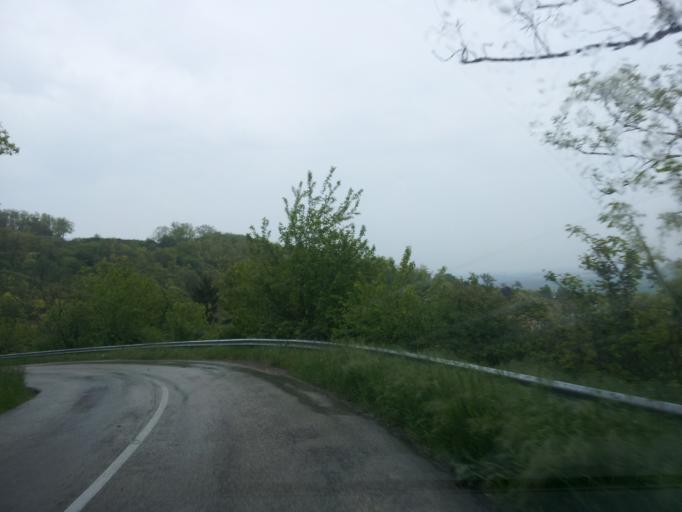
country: HU
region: Tolna
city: Szekszard
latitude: 46.2979
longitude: 18.6788
